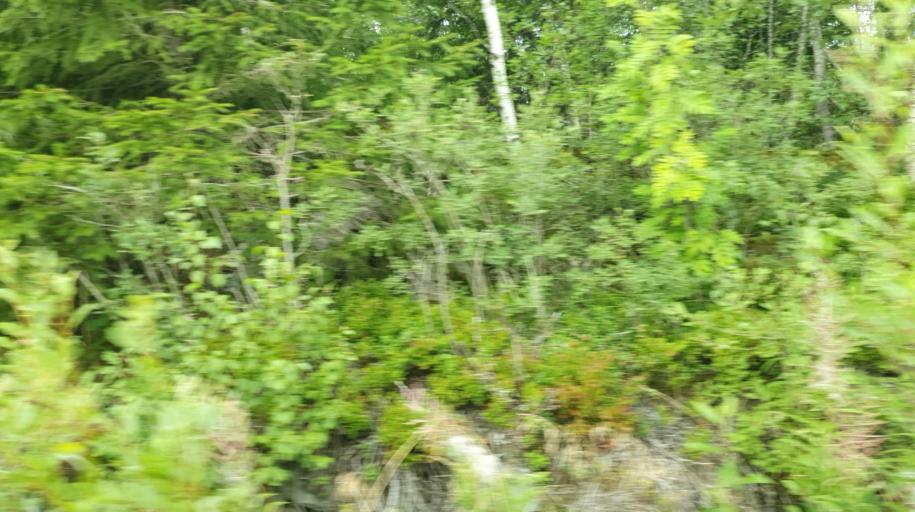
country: NO
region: Sor-Trondelag
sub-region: Selbu
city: Mebonden
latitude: 63.2567
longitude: 11.0876
